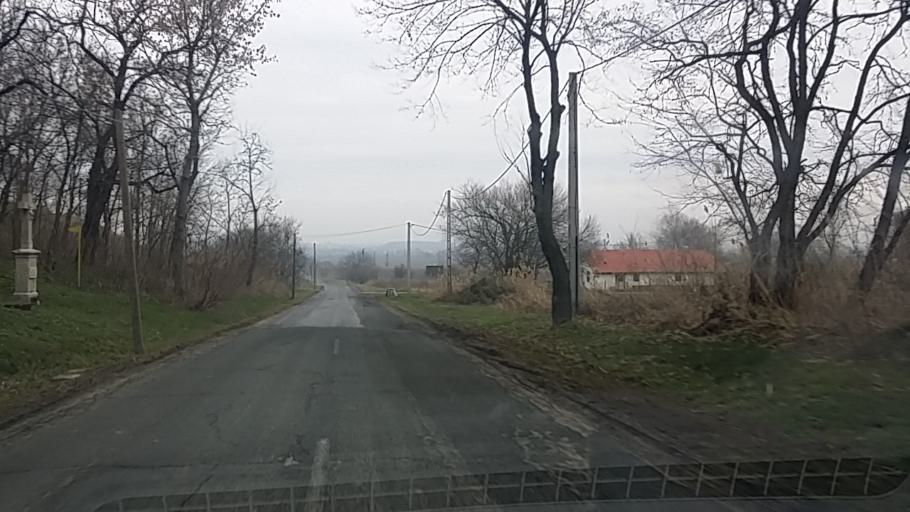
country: HU
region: Komarom-Esztergom
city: Tat
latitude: 47.7316
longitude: 18.6164
